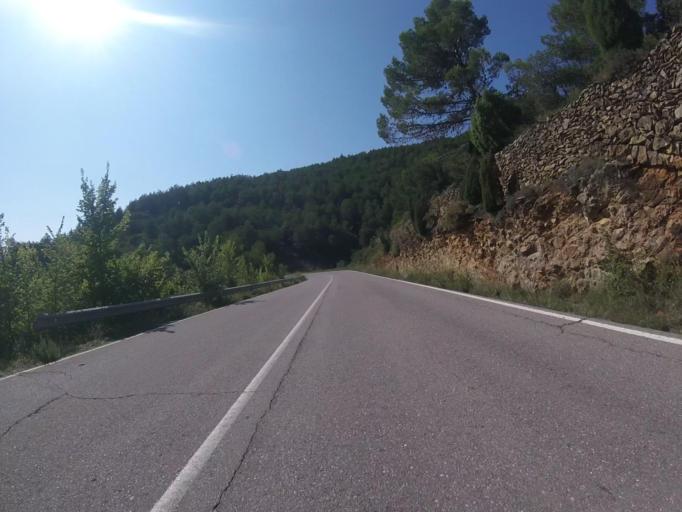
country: ES
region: Valencia
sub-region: Provincia de Castello
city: Benafigos
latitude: 40.2674
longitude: -0.2368
